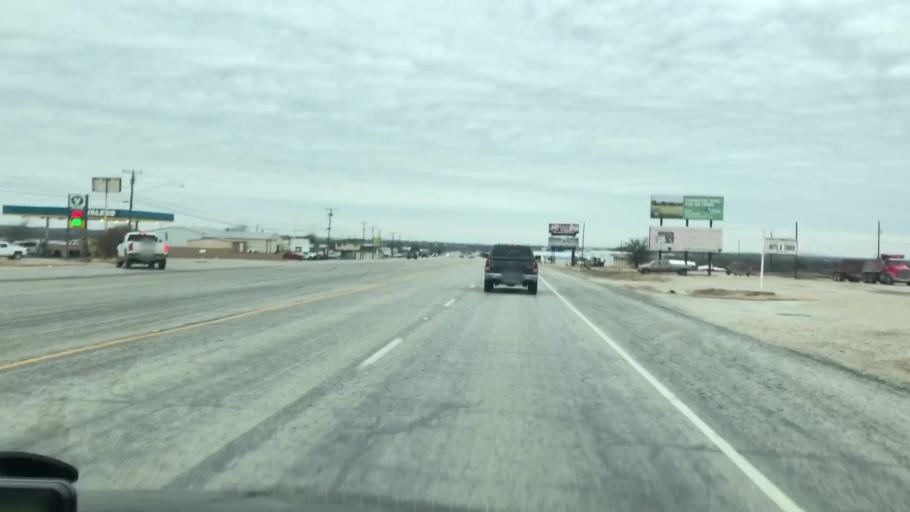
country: US
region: Texas
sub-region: Jack County
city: Jacksboro
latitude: 33.1979
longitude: -98.1471
